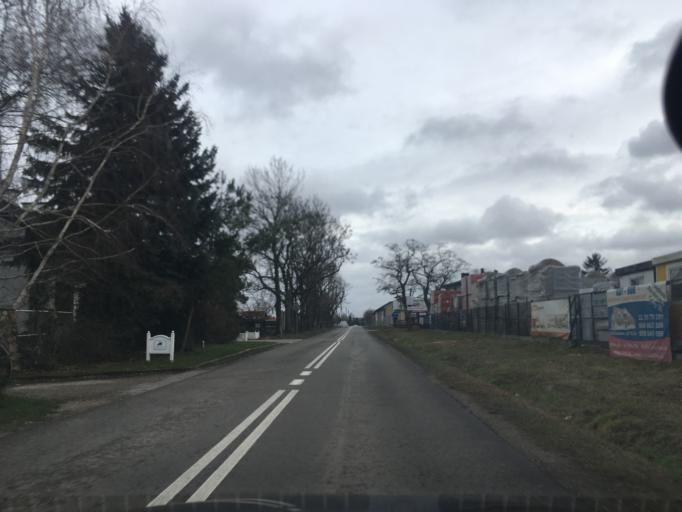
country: PL
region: Masovian Voivodeship
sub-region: Powiat piaseczynski
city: Lesznowola
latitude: 52.1199
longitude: 20.9398
